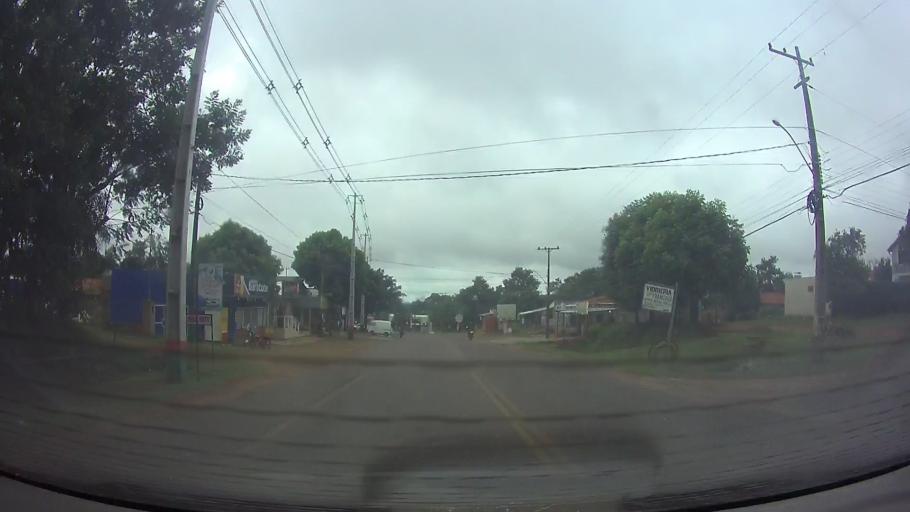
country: PY
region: Cordillera
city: Altos
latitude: -25.2690
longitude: -57.2535
